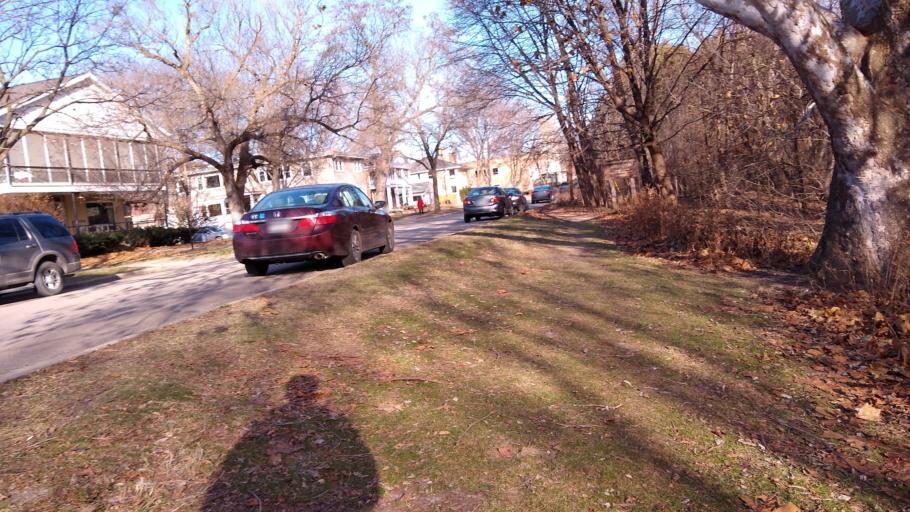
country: US
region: Wisconsin
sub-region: Dane County
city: Shorewood Hills
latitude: 43.0552
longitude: -89.4300
